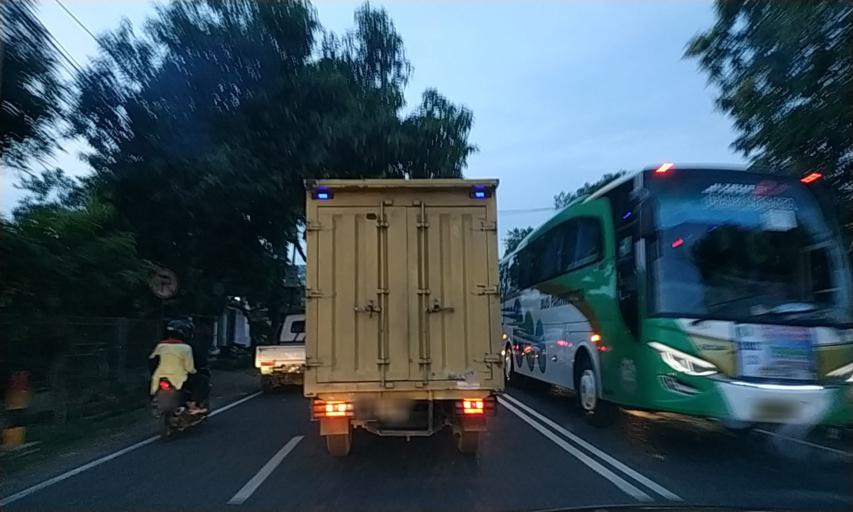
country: ID
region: Daerah Istimewa Yogyakarta
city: Srandakan
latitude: -7.8448
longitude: 110.2182
